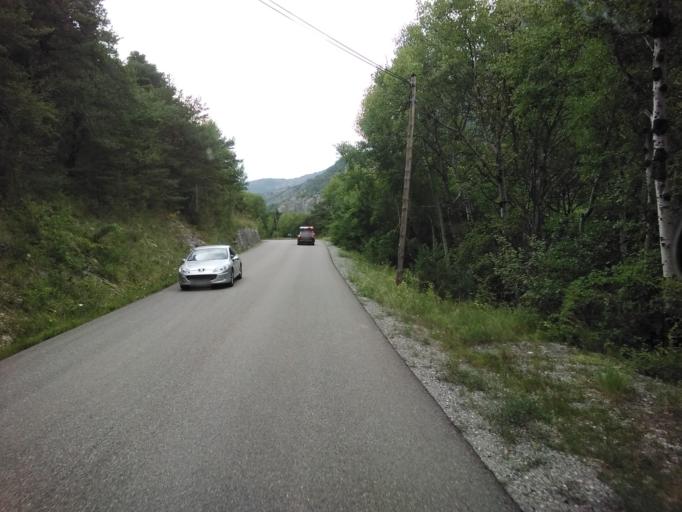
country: FR
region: Provence-Alpes-Cote d'Azur
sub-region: Departement des Alpes-de-Haute-Provence
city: Seyne-les-Alpes
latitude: 44.4470
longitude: 6.4064
